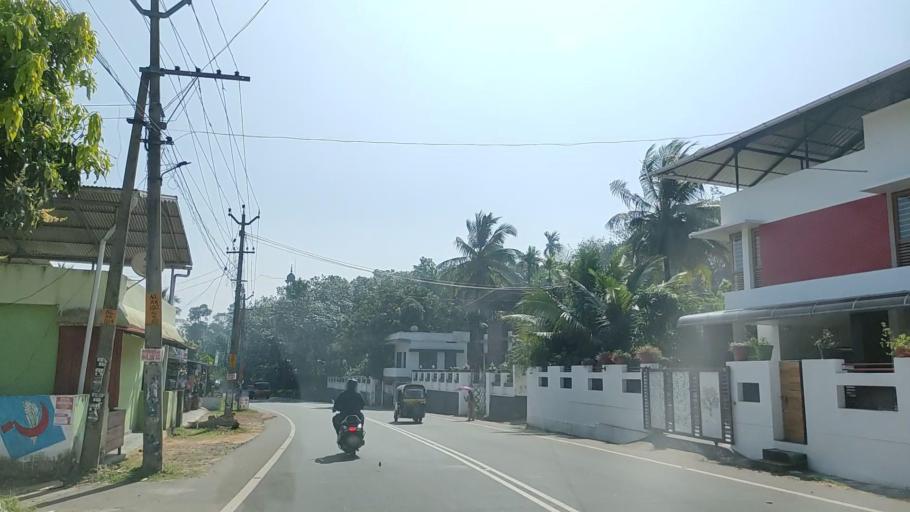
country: IN
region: Kerala
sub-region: Kollam
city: Punalur
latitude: 8.9352
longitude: 76.9487
